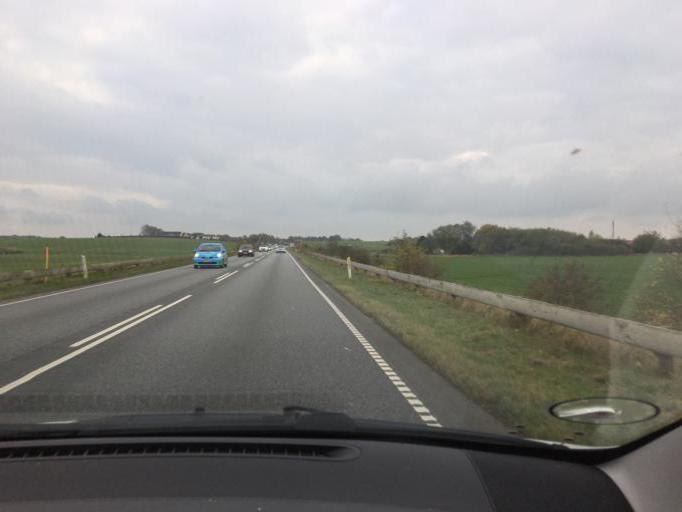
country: DK
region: South Denmark
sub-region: Fredericia Kommune
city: Fredericia
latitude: 55.6126
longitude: 9.7519
